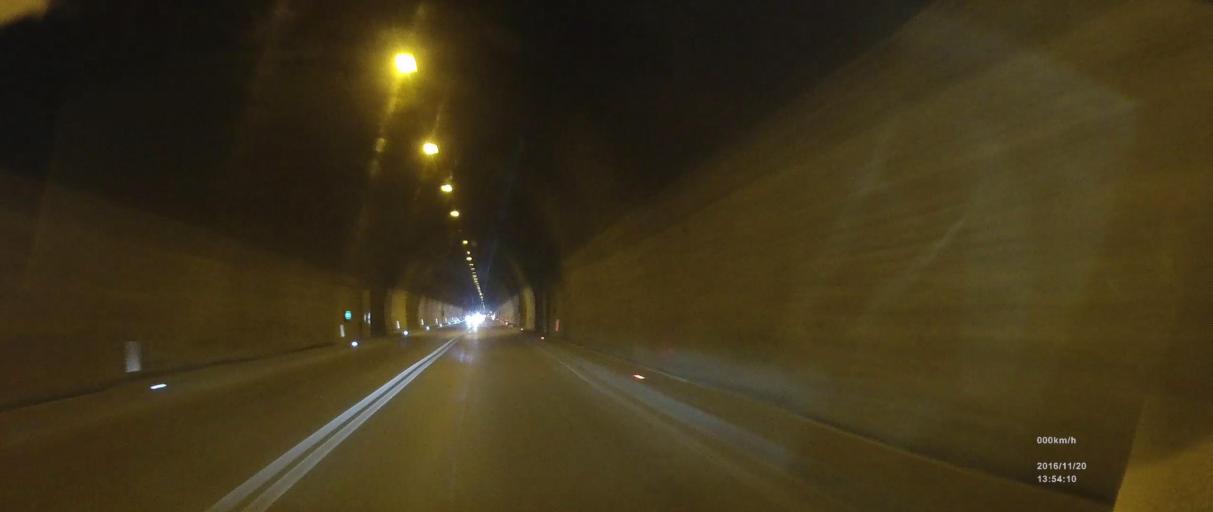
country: HR
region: Splitsko-Dalmatinska
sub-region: Grad Split
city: Split
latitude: 43.5102
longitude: 16.4264
